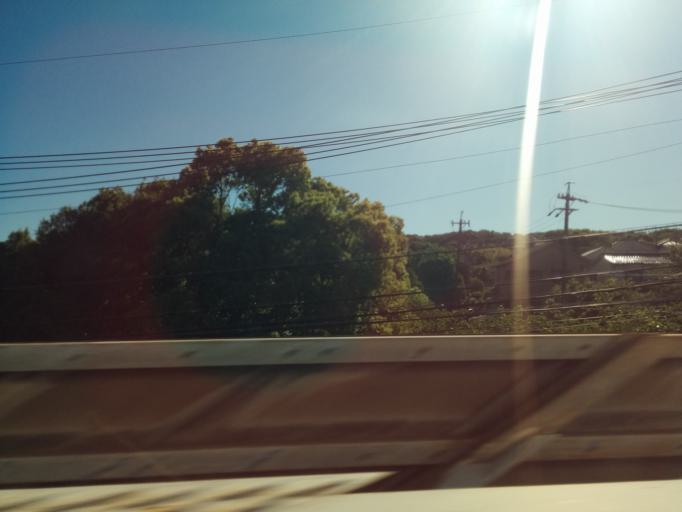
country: JP
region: Aichi
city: Obu
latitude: 35.0614
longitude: 136.9452
